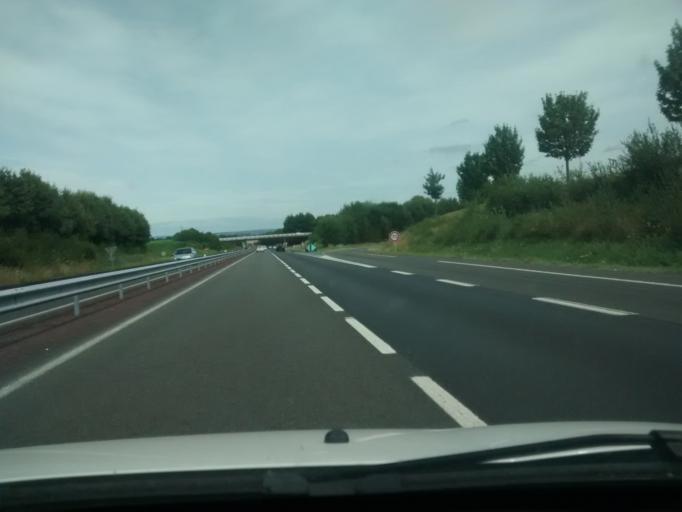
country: FR
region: Lower Normandy
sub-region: Departement de la Manche
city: Saint-James
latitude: 48.5270
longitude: -1.3453
